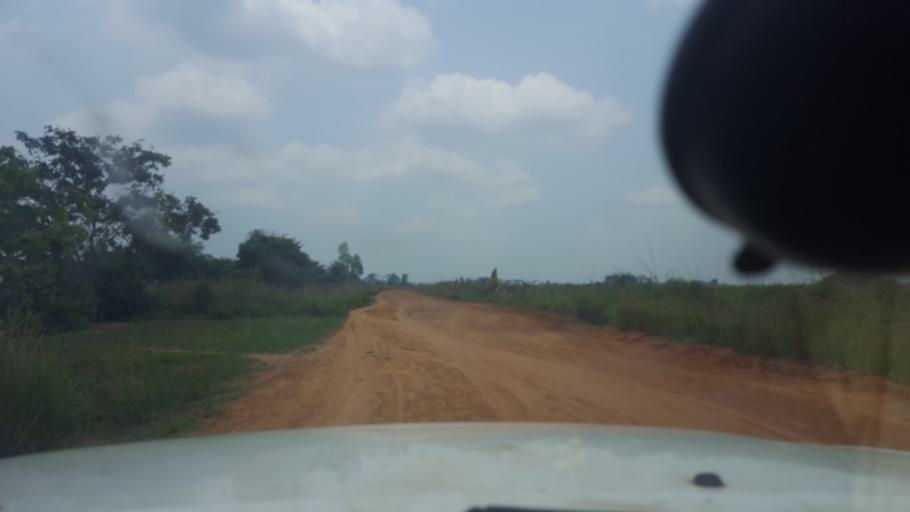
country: CD
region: Bandundu
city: Bandundu
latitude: -3.3284
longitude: 17.2895
